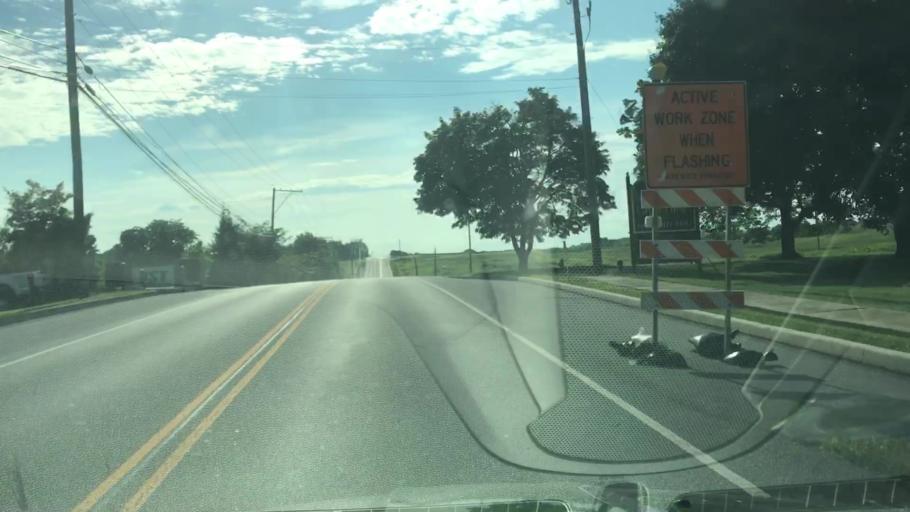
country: US
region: Pennsylvania
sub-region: Dauphin County
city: Highspire
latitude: 40.2273
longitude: -76.7655
